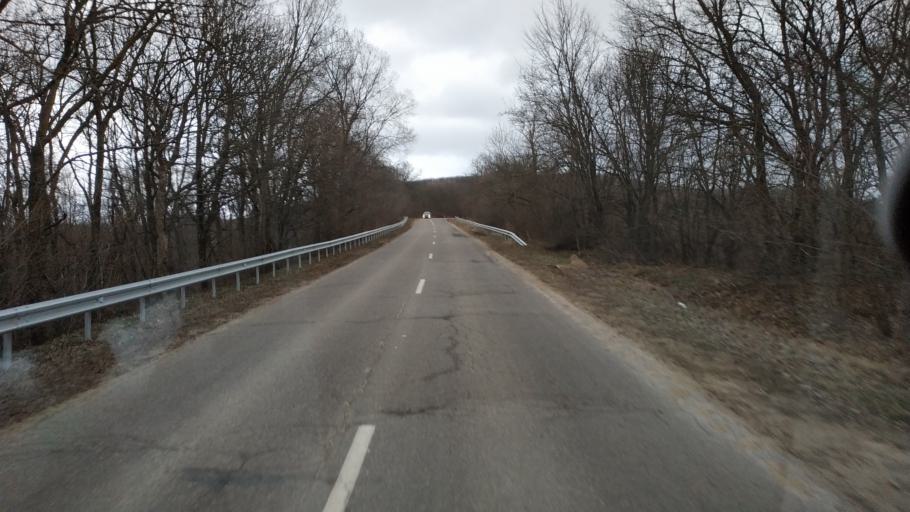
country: MD
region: Calarasi
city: Calarasi
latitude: 47.2287
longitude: 28.2747
